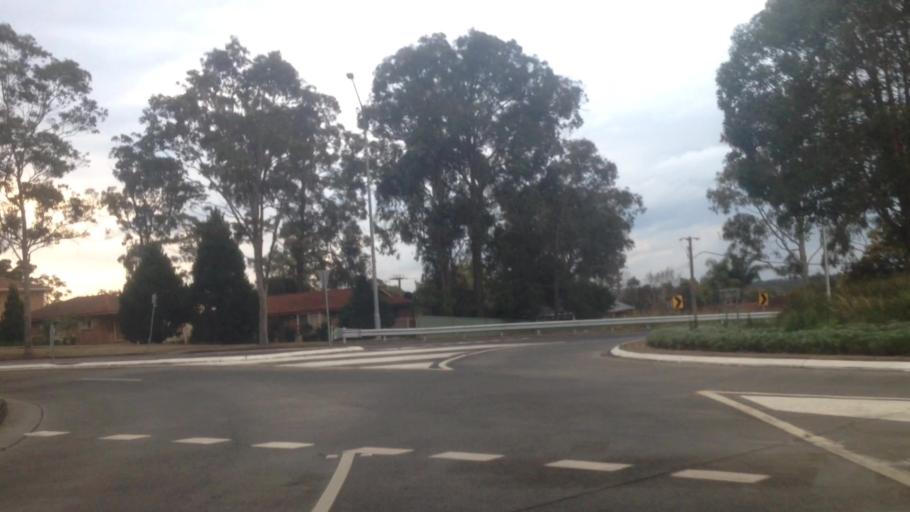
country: AU
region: New South Wales
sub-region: Wyong Shire
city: Jilliby
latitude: -33.2681
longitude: 151.4318
